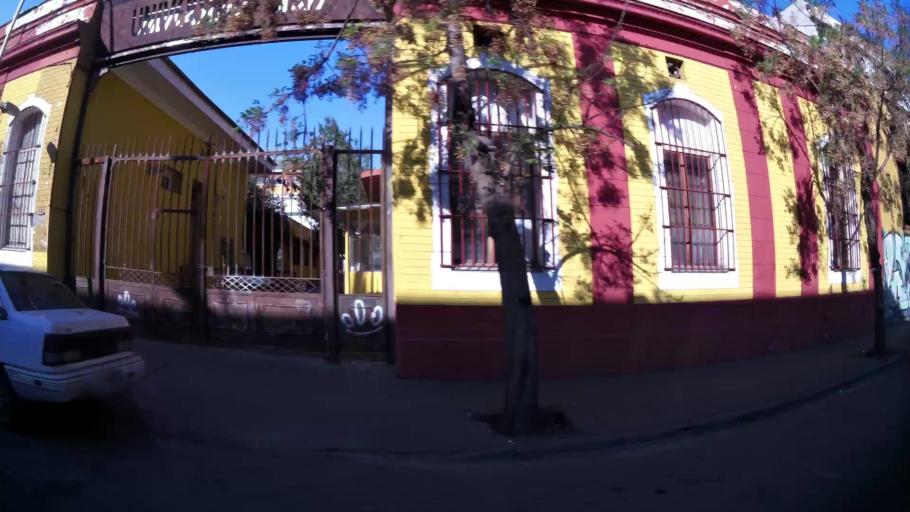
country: CL
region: Santiago Metropolitan
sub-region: Provincia de Santiago
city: Santiago
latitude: -33.4464
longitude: -70.6735
